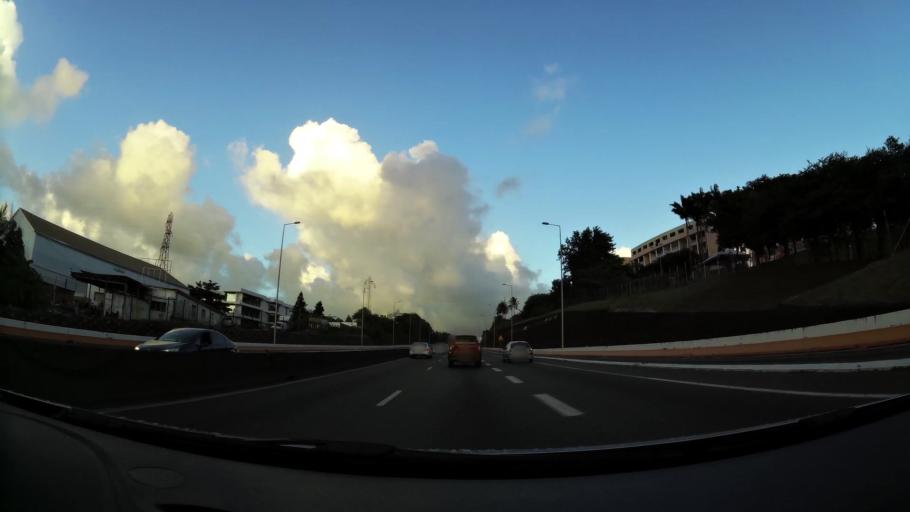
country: MQ
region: Martinique
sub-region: Martinique
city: Fort-de-France
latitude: 14.6158
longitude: -61.0440
